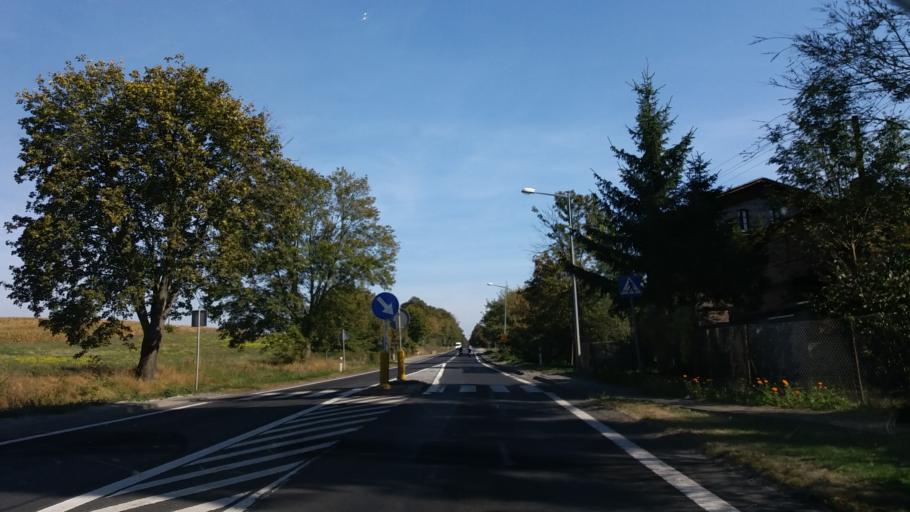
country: PL
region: Greater Poland Voivodeship
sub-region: Powiat miedzychodzki
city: Kwilcz
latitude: 52.5639
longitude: 16.0035
